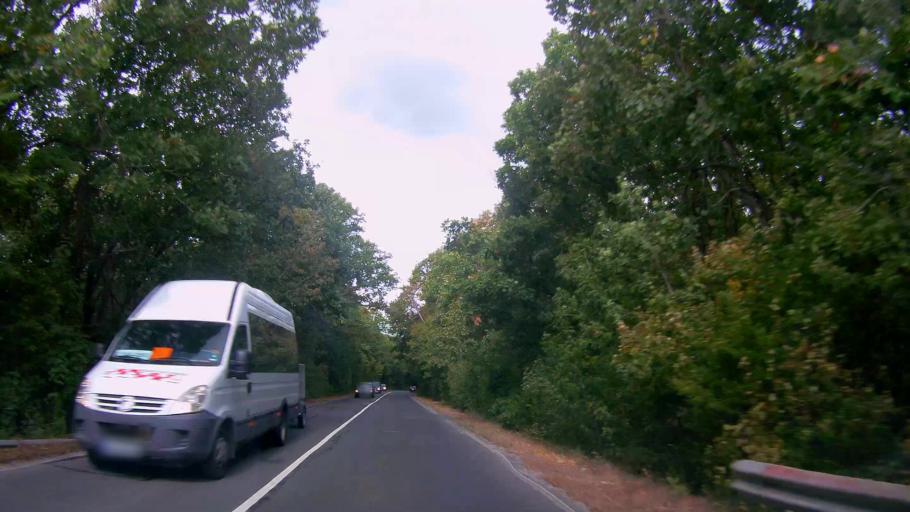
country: BG
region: Burgas
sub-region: Obshtina Primorsko
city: Primorsko
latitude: 42.2927
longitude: 27.7318
